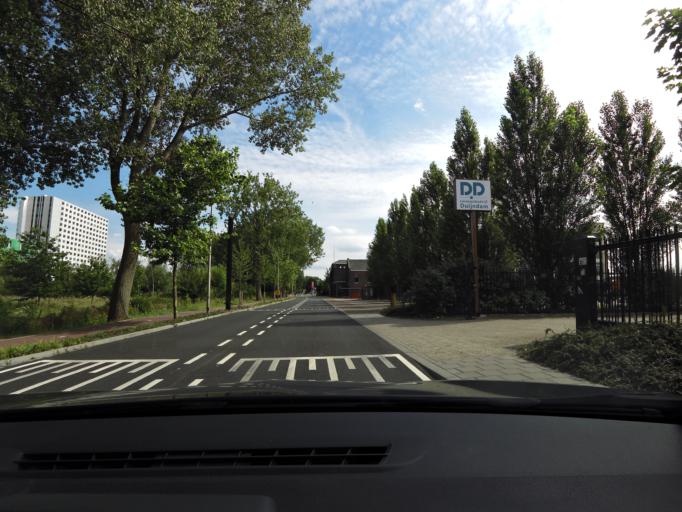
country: NL
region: South Holland
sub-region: Gemeente Delft
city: Delft
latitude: 51.9974
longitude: 4.3697
